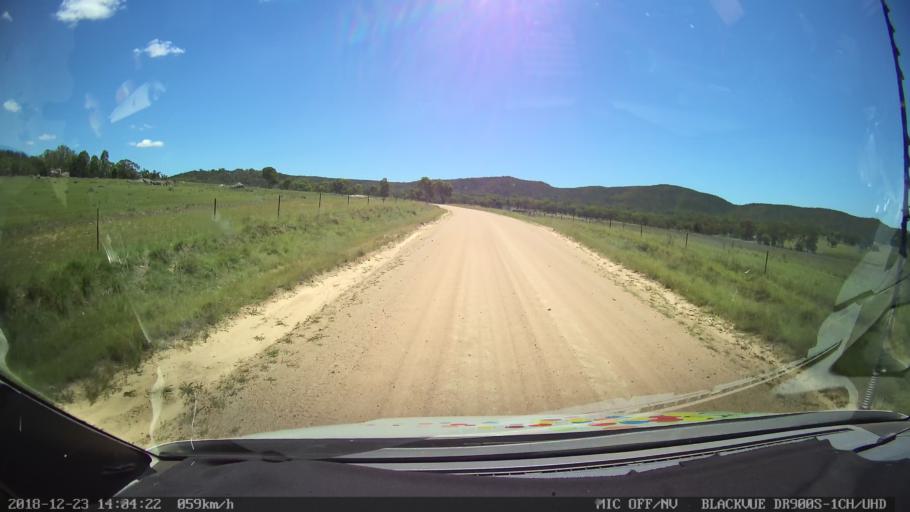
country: AU
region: New South Wales
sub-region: Tamworth Municipality
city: Manilla
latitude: -30.6225
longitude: 151.0914
